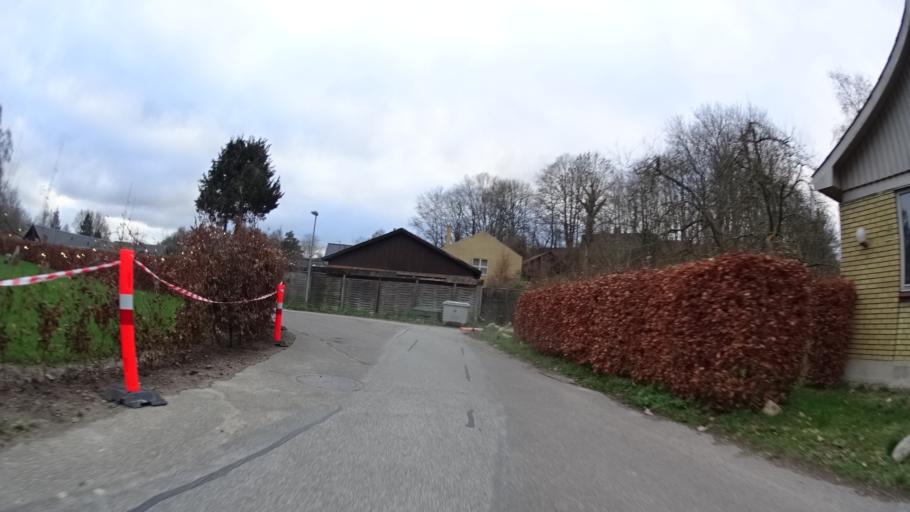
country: DK
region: Central Jutland
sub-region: Arhus Kommune
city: Stavtrup
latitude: 56.1610
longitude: 10.1203
